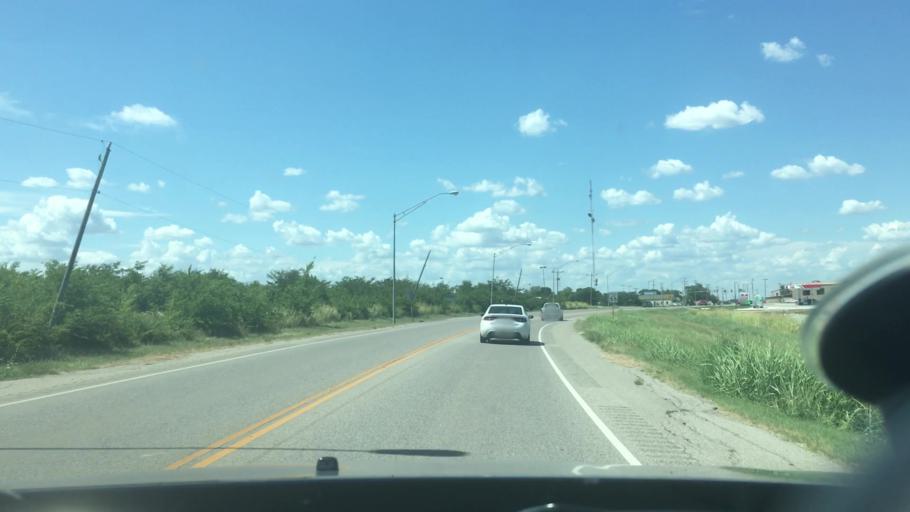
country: US
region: Oklahoma
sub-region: Marshall County
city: Madill
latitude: 34.0668
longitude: -96.7626
